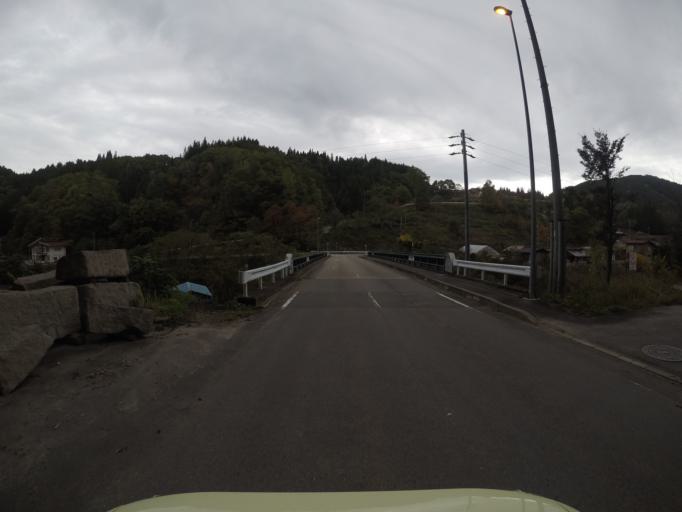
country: JP
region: Gifu
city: Takayama
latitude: 36.1391
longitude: 137.3504
